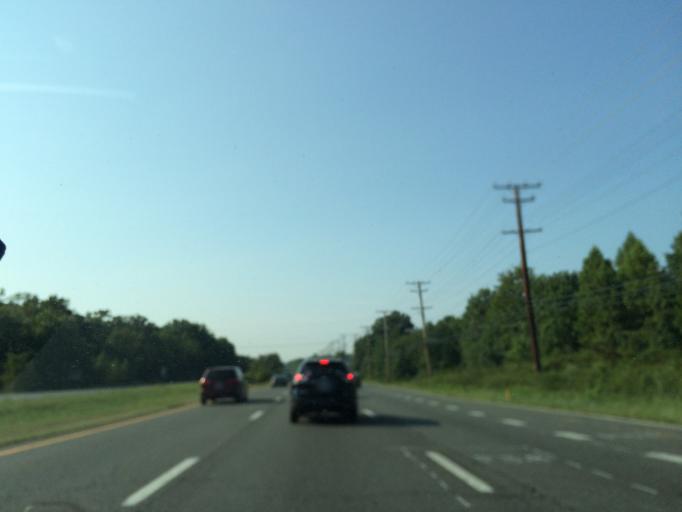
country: US
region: Maryland
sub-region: Prince George's County
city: Bowie
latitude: 38.9411
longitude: -76.7181
